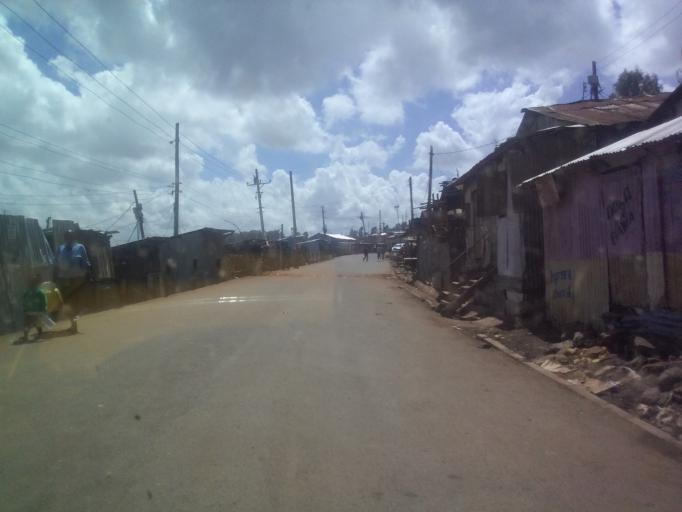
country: KE
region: Nairobi Area
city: Nairobi
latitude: -1.3168
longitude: 36.7775
